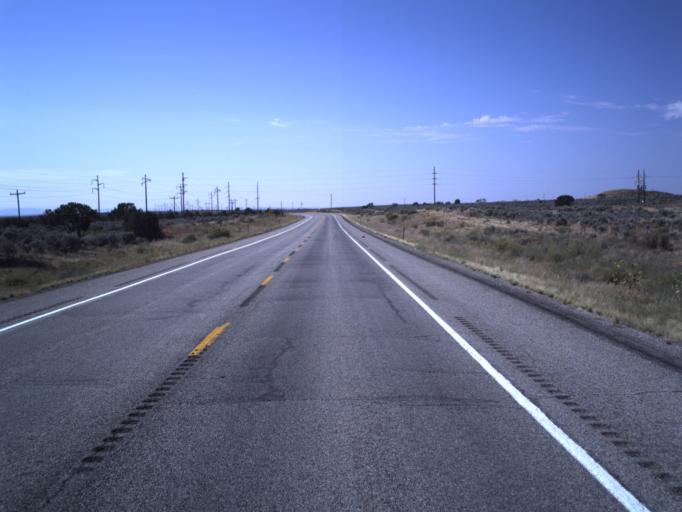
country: US
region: Utah
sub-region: San Juan County
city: Blanding
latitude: 37.5417
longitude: -109.4930
